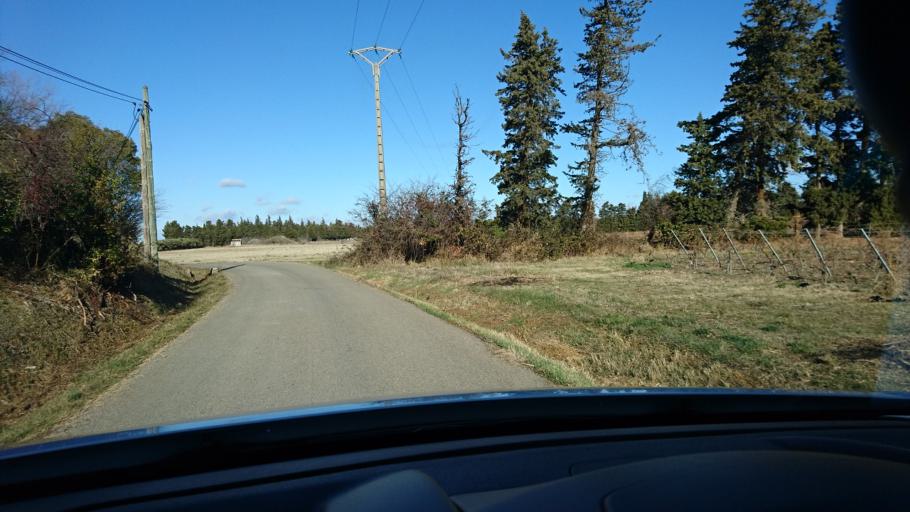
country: FR
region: Provence-Alpes-Cote d'Azur
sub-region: Departement des Bouches-du-Rhone
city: Noves
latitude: 43.9004
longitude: 4.9136
